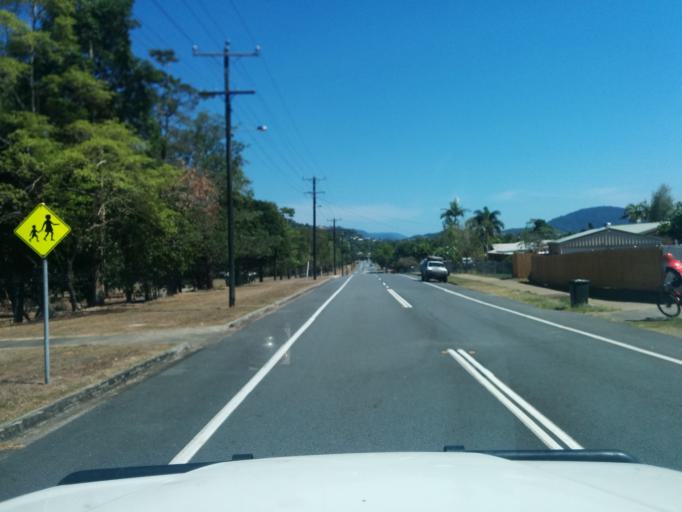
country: AU
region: Queensland
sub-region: Cairns
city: Woree
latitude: -16.9528
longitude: 145.7365
